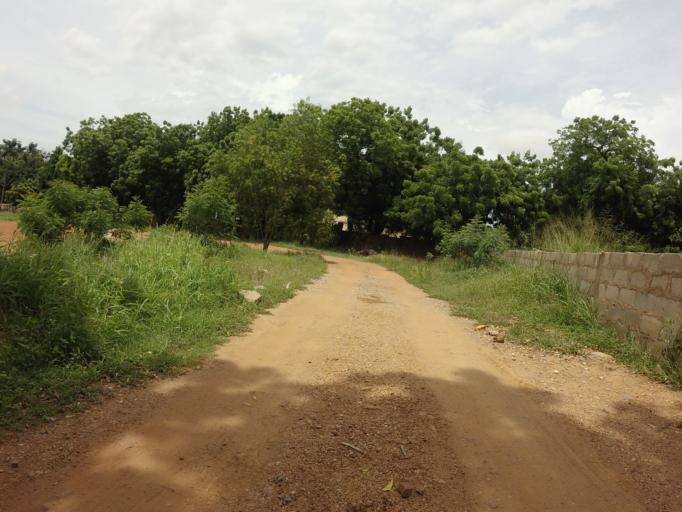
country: GH
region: Greater Accra
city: Accra
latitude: 5.5952
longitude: -0.2232
